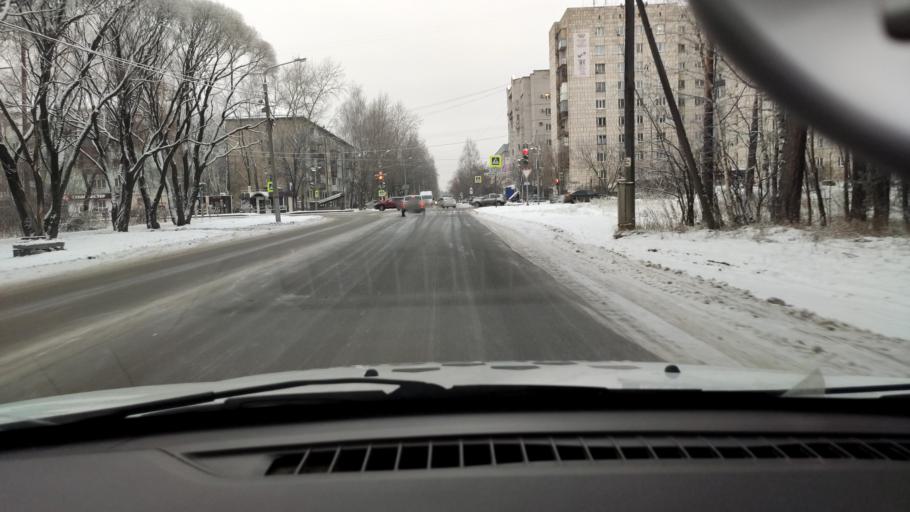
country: RU
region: Perm
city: Kultayevo
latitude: 58.0154
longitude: 55.9815
